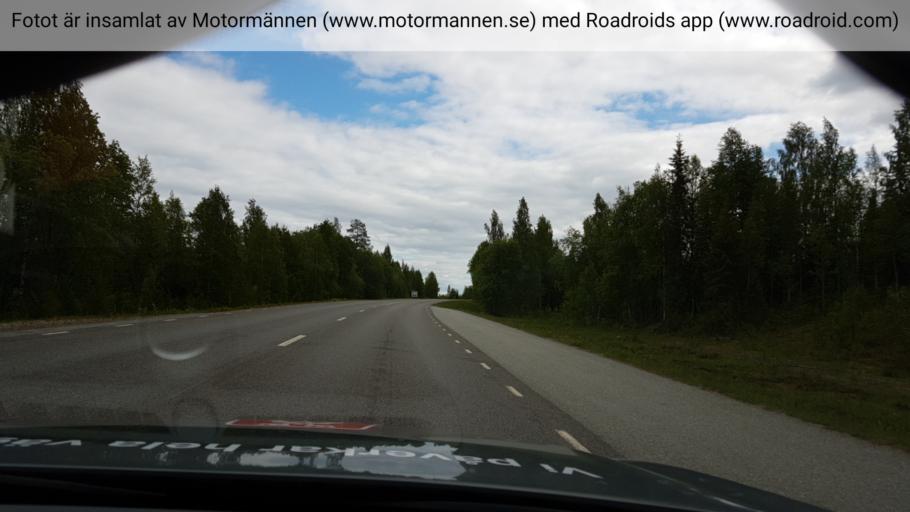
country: SE
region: Jaemtland
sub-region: Stroemsunds Kommun
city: Stroemsund
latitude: 64.3155
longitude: 15.2126
